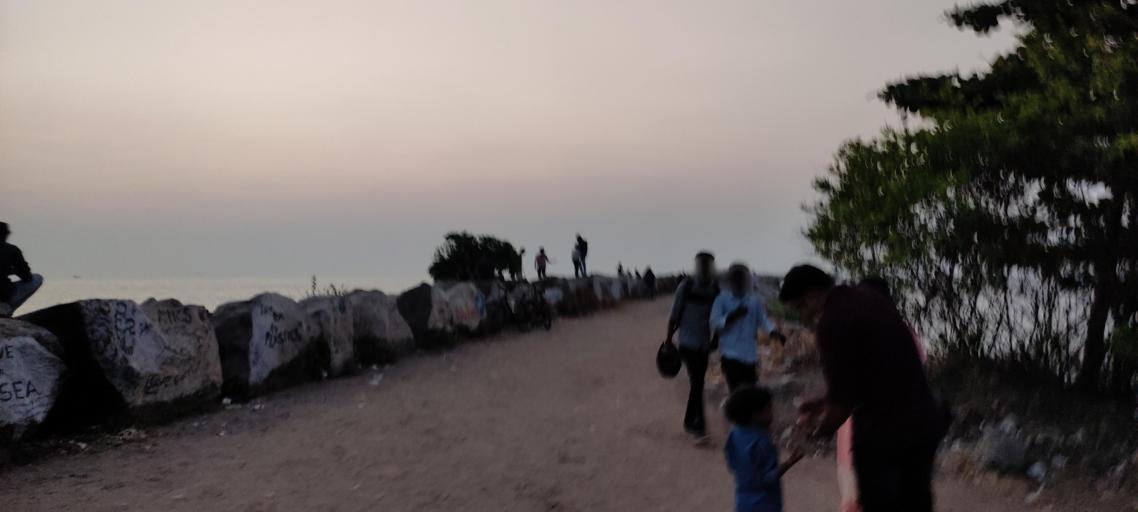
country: IN
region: Kerala
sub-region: Alappuzha
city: Kayankulam
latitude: 9.1346
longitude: 76.4634
